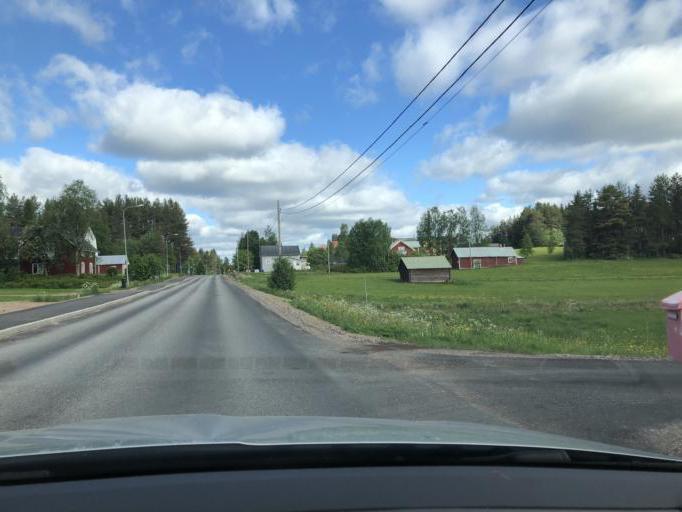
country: SE
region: Norrbotten
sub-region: Pajala Kommun
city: Pajala
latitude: 67.2215
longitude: 23.3467
